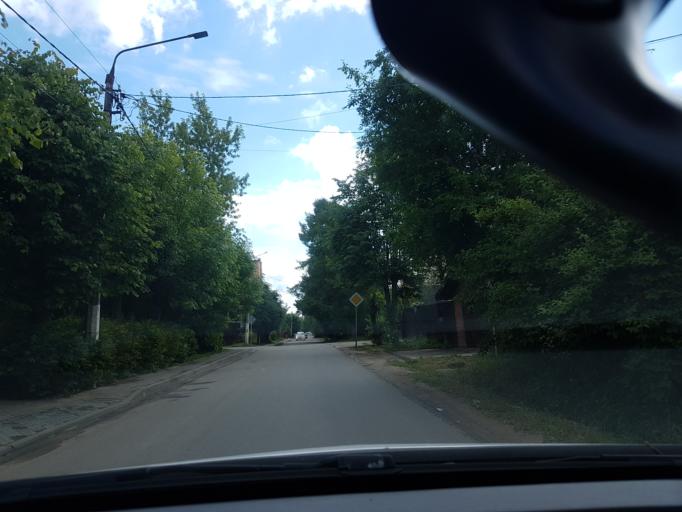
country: RU
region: Moskovskaya
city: Istra
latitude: 55.9173
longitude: 36.8753
